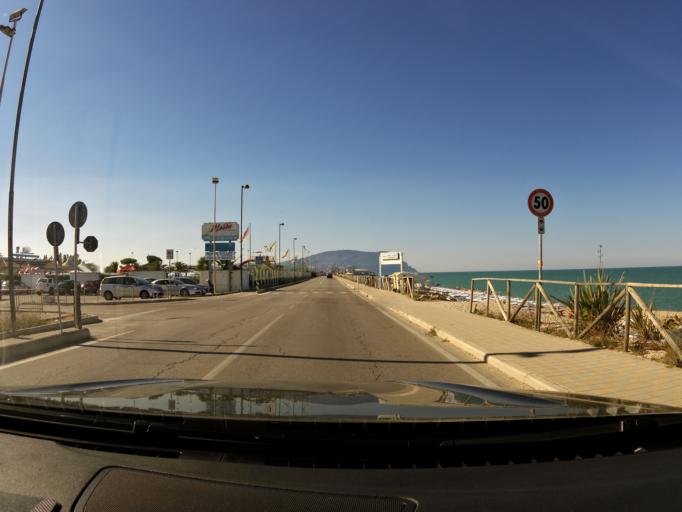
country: IT
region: The Marches
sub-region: Provincia di Macerata
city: Porto Recanati
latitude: 43.4533
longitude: 13.6530
